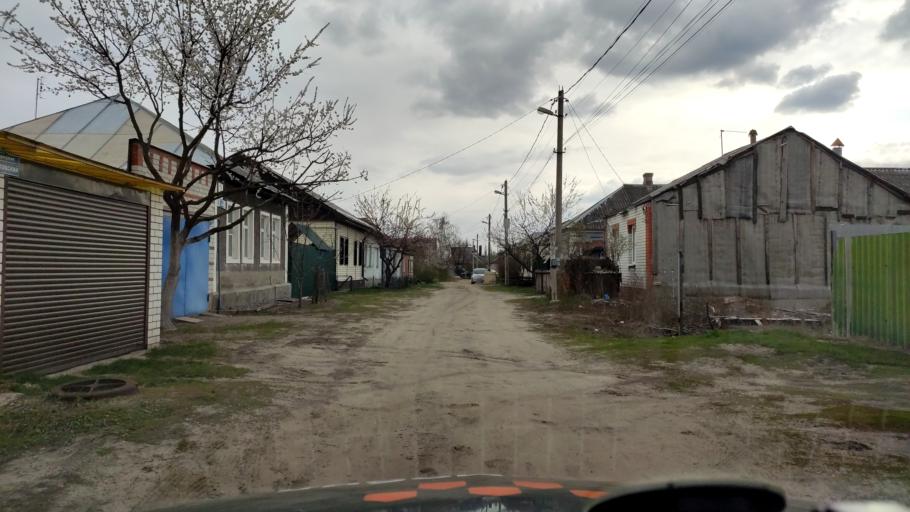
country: RU
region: Voronezj
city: Somovo
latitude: 51.7429
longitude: 39.2736
